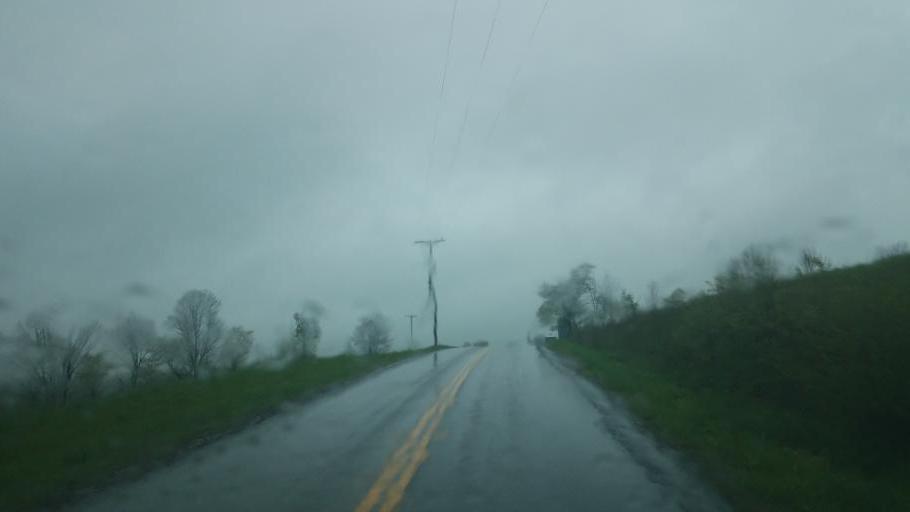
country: US
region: Pennsylvania
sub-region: Tioga County
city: Westfield
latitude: 42.0827
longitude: -77.4898
